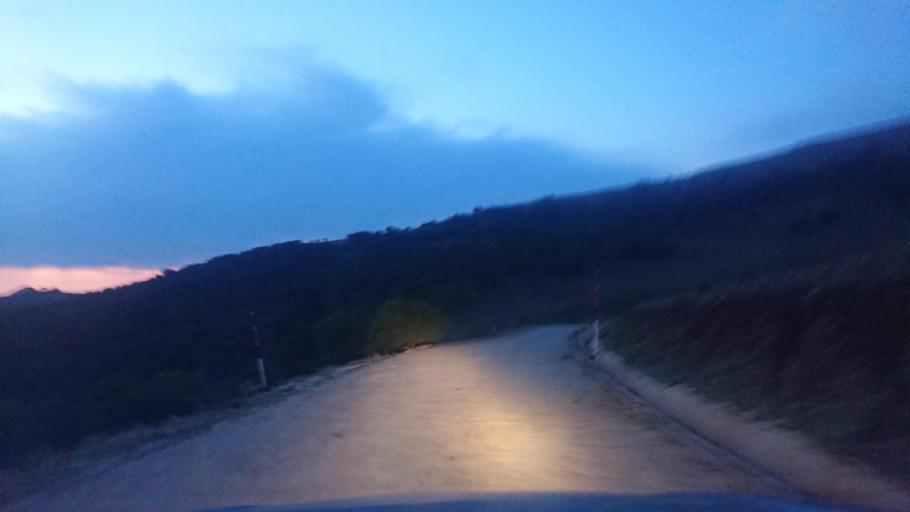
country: TR
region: Aksaray
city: Ortakoy
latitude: 38.6425
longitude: 34.0247
